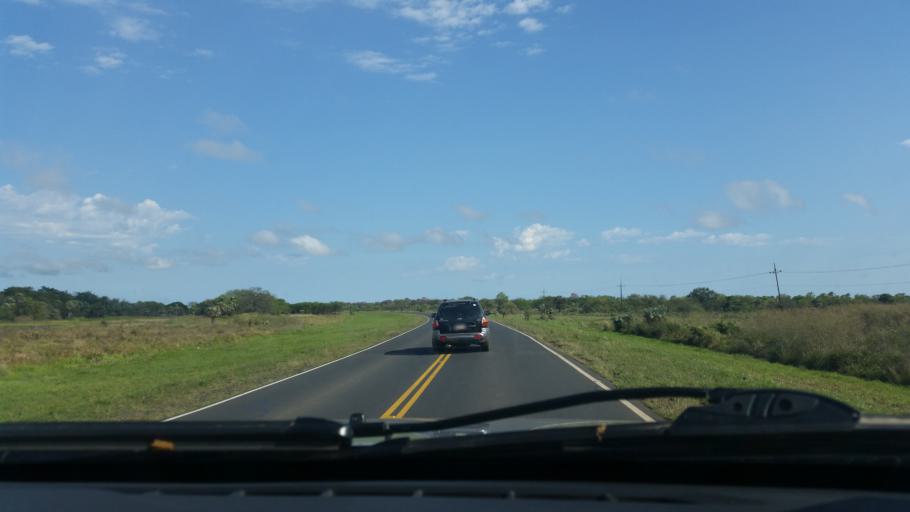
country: PY
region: Presidente Hayes
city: Benjamin Aceval
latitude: -24.9244
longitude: -57.5709
